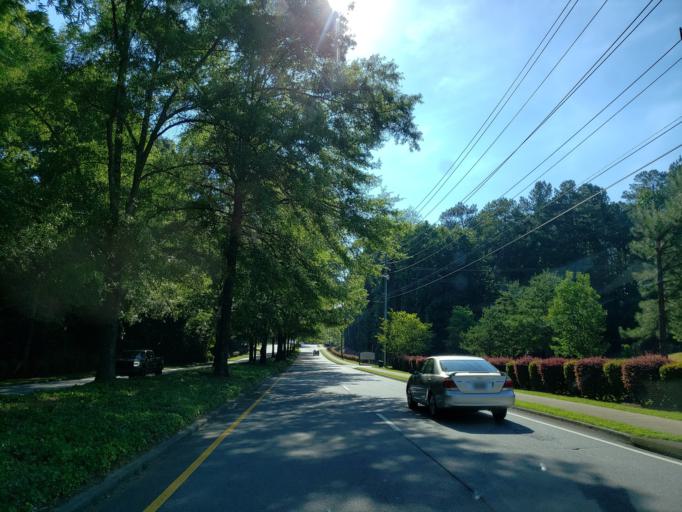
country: US
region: Georgia
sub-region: Cherokee County
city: Woodstock
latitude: 34.1286
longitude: -84.5820
